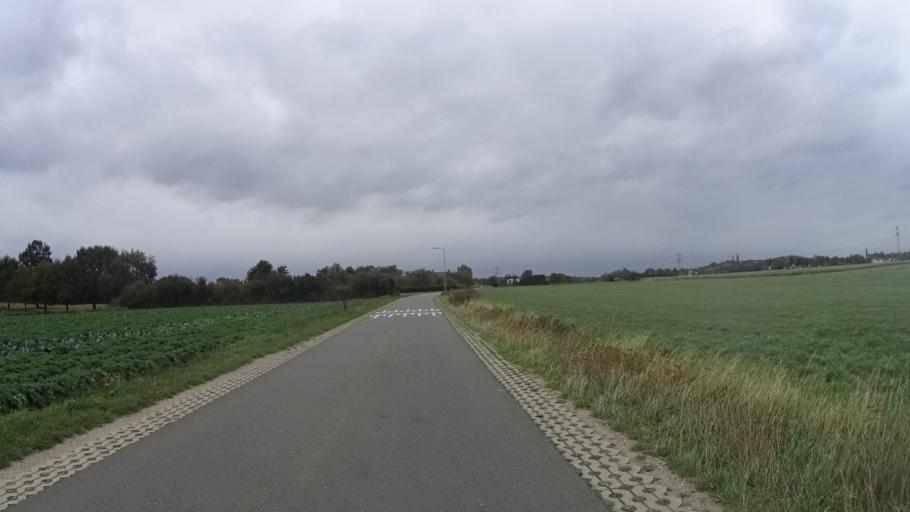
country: NL
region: Limburg
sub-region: Gemeente Venlo
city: Tegelen
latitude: 51.3253
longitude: 6.1081
